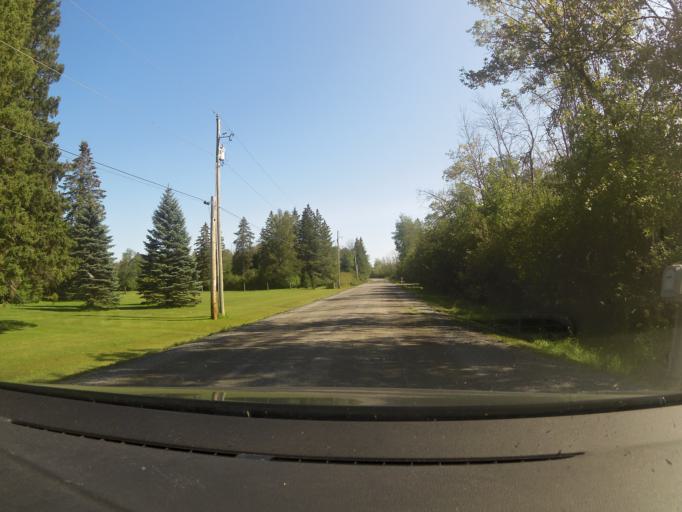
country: CA
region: Ontario
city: Carleton Place
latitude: 45.3189
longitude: -76.0742
